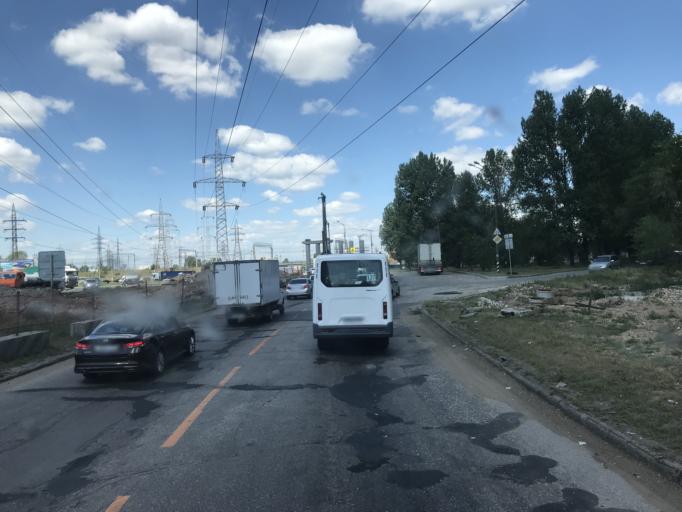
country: RU
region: Samara
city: Zhigulevsk
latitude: 53.4783
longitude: 49.5120
